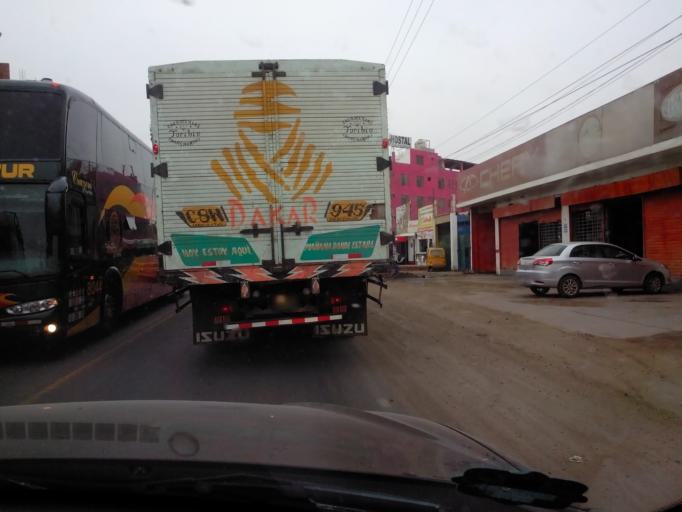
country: PE
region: Ica
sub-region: Provincia de Chincha
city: Chincha Alta
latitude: -13.4223
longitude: -76.1361
